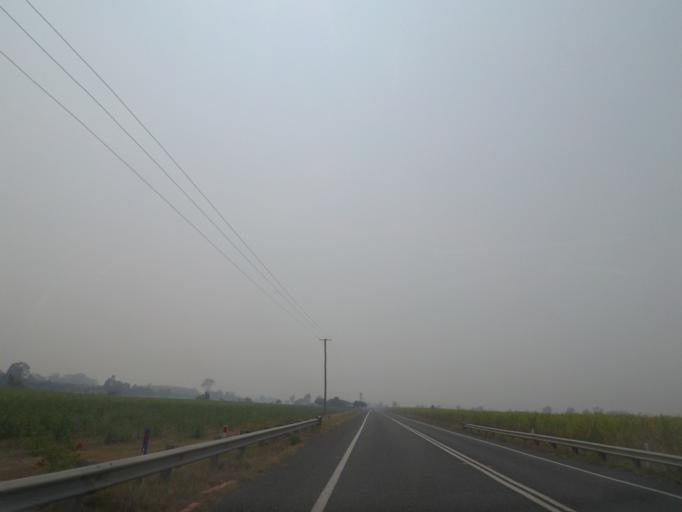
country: AU
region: New South Wales
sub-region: Clarence Valley
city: Maclean
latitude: -29.5647
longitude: 153.1131
